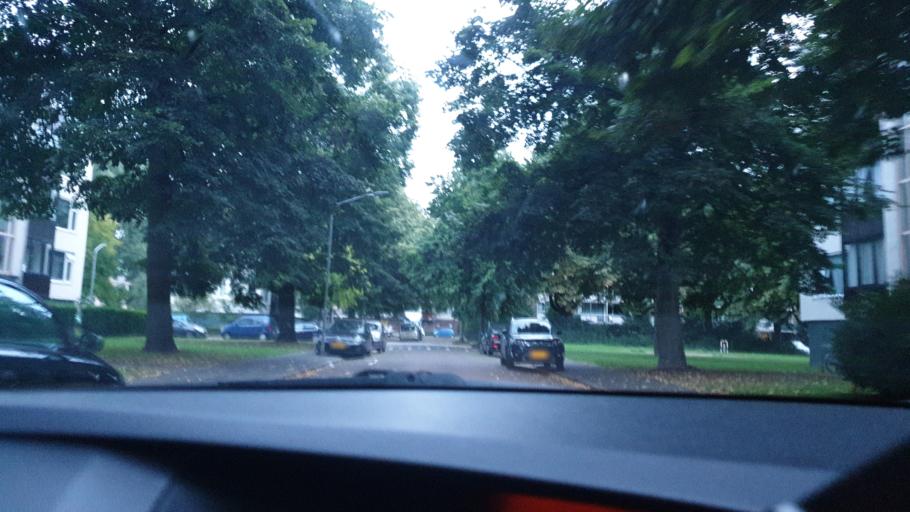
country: NL
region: South Holland
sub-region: Gemeente Dordrecht
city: Dordrecht
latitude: 51.7881
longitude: 4.6614
